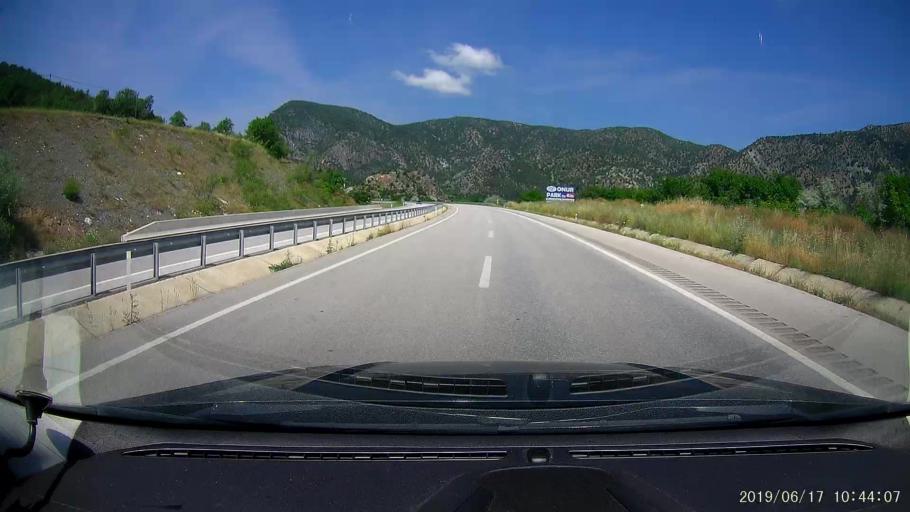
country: TR
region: Corum
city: Kargi
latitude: 41.0716
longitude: 34.5208
